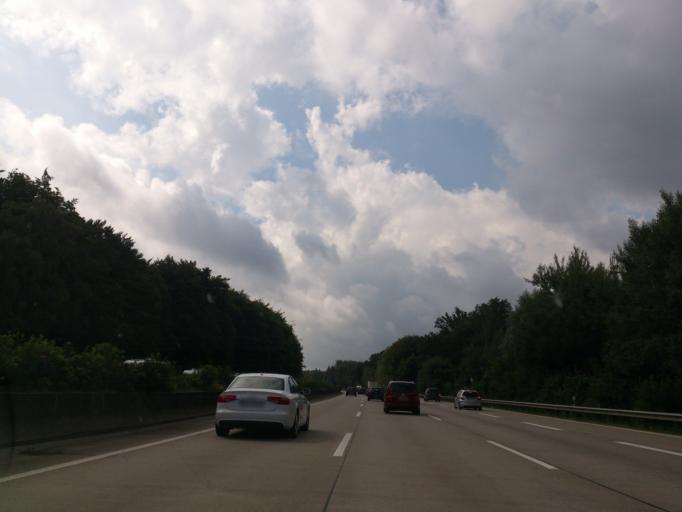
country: DE
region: Lower Saxony
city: Garlstorf
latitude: 53.2305
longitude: 10.0765
